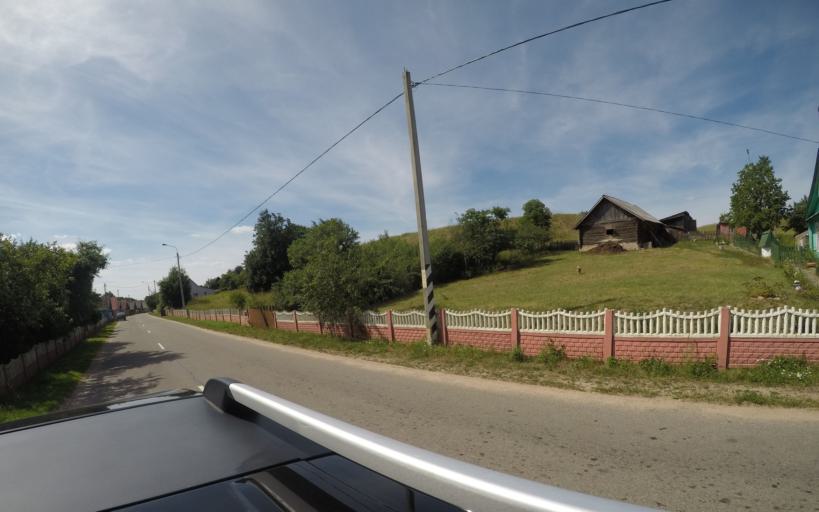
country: BY
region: Grodnenskaya
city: Hal'shany
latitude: 54.2593
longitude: 26.0016
